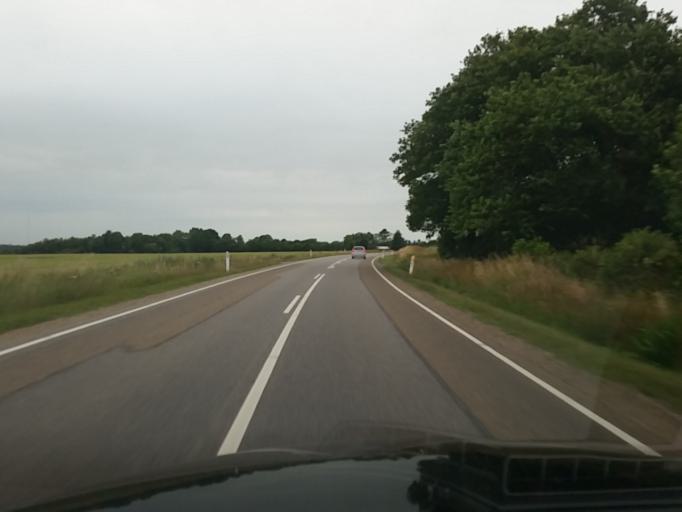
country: DK
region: South Denmark
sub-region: Billund Kommune
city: Grindsted
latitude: 55.6593
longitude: 8.7826
